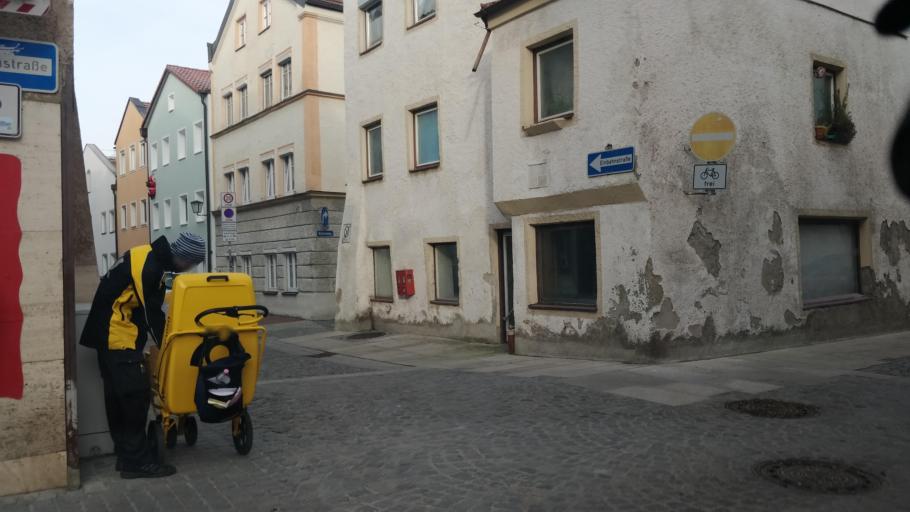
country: DE
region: Bavaria
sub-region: Upper Bavaria
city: Muehldorf
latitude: 48.2419
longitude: 12.5261
